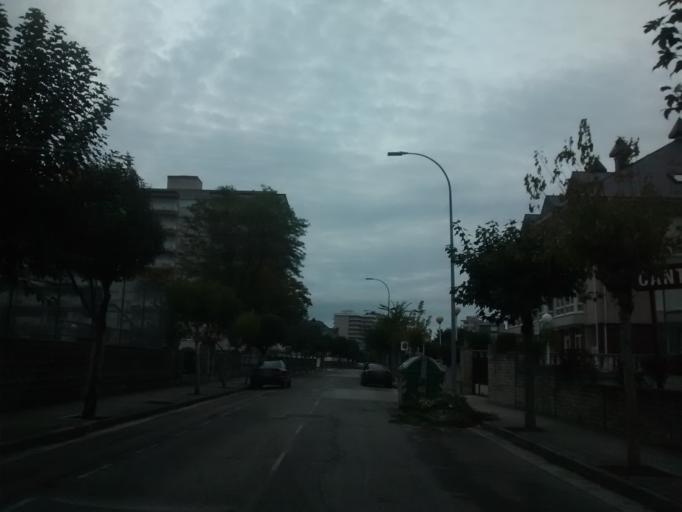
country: ES
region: Cantabria
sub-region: Provincia de Cantabria
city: Laredo
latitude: 43.4103
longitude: -3.4301
